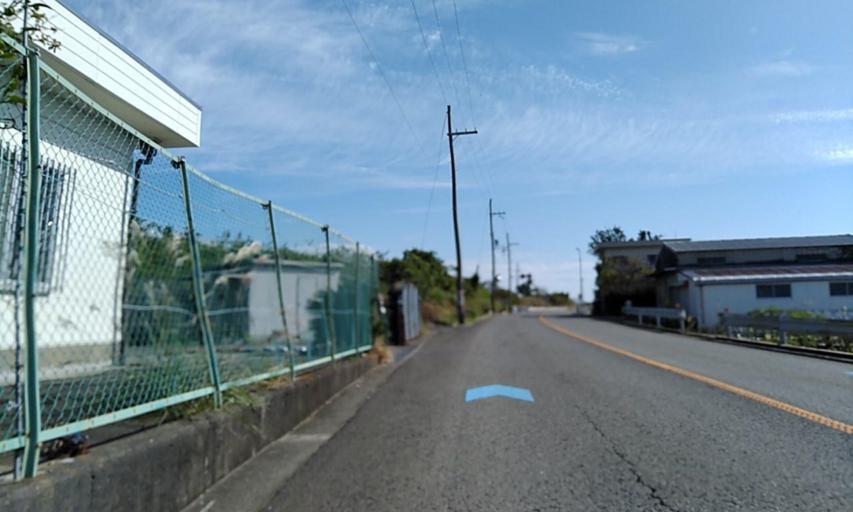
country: JP
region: Wakayama
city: Gobo
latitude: 33.8253
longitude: 135.1894
